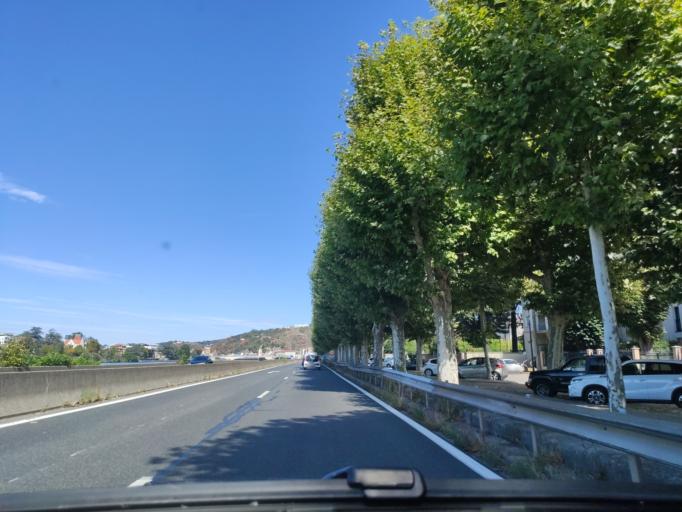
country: FR
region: Rhone-Alpes
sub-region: Departement de l'Isere
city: Vienne
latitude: 45.5165
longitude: 4.8633
